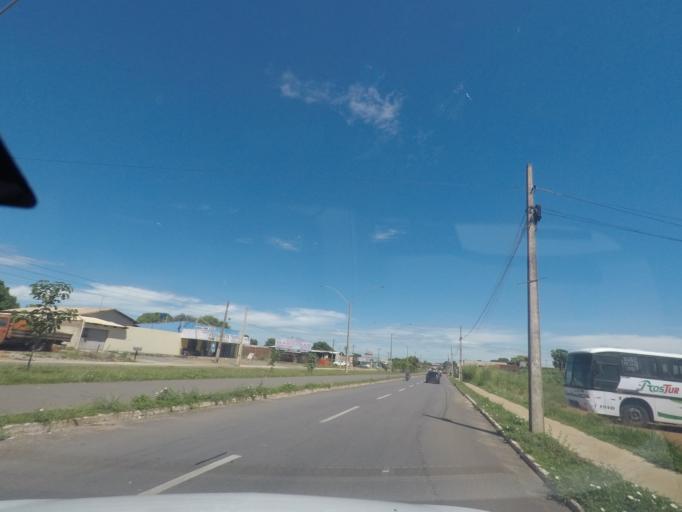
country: BR
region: Goias
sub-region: Aparecida De Goiania
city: Aparecida de Goiania
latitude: -16.7825
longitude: -49.3318
